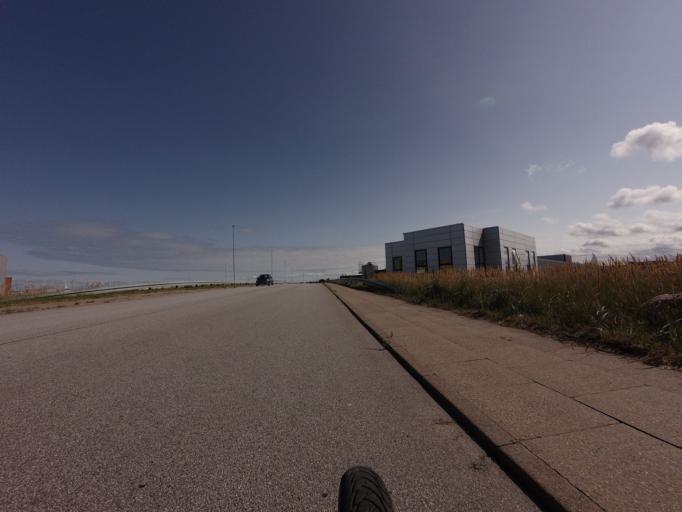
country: DK
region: North Denmark
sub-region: Hjorring Kommune
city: Hirtshals
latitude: 57.5880
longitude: 9.9733
